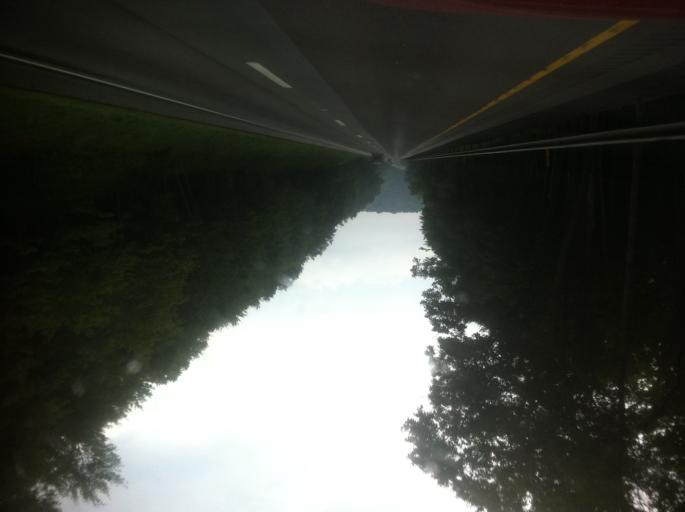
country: US
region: Pennsylvania
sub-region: Jefferson County
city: Brookville
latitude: 41.1535
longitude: -78.9974
